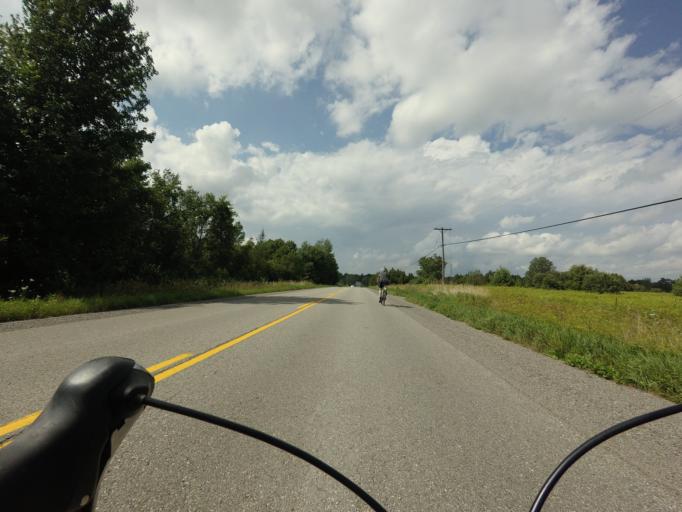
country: CA
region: Ontario
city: Brockville
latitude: 44.6960
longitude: -75.7453
